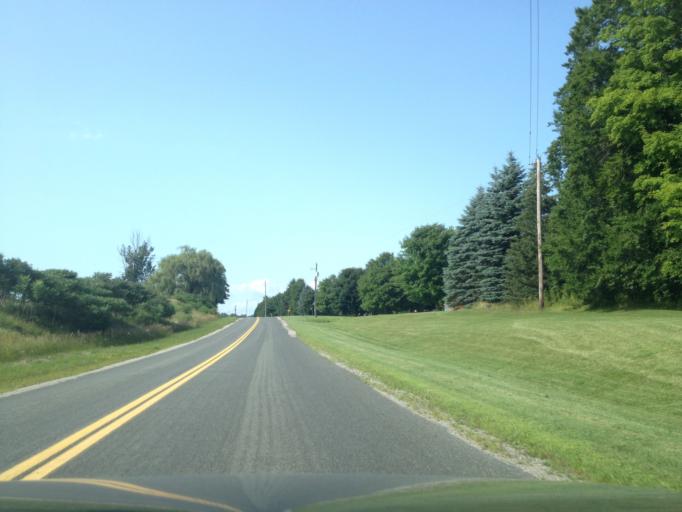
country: CA
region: Ontario
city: Aylmer
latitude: 42.7369
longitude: -80.8535
